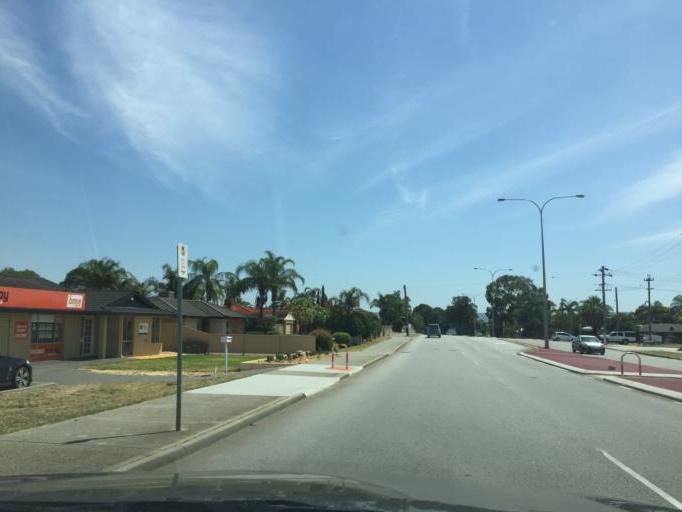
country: AU
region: Western Australia
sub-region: Gosnells
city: Thornlie
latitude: -32.0716
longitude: 115.9657
